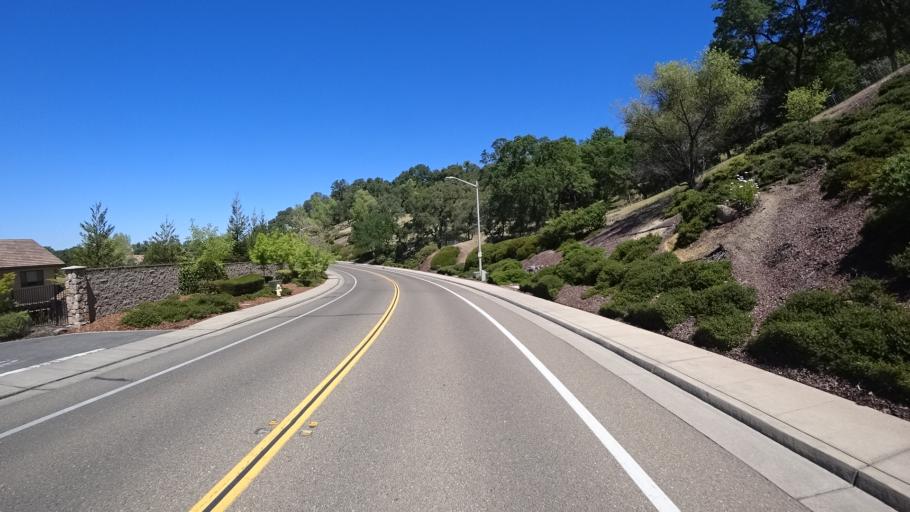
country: US
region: California
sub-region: Placer County
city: Rocklin
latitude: 38.8302
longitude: -121.2467
